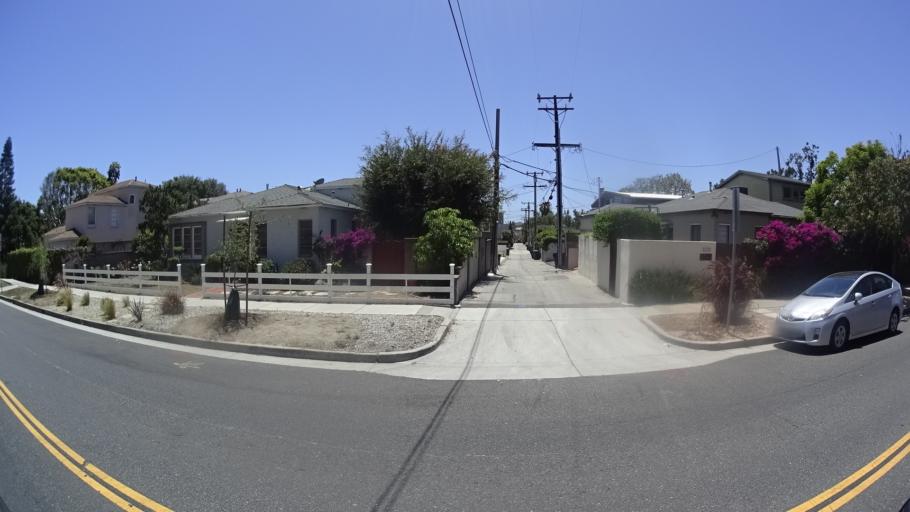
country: US
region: California
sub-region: Los Angeles County
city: Santa Monica
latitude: 34.0116
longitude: -118.4770
